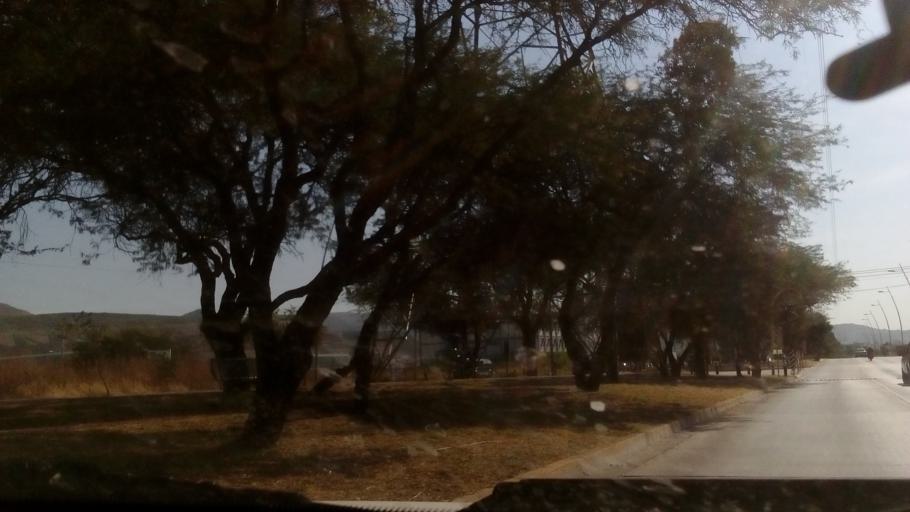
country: MX
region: Guanajuato
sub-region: Leon
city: Medina
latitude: 21.1346
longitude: -101.6148
